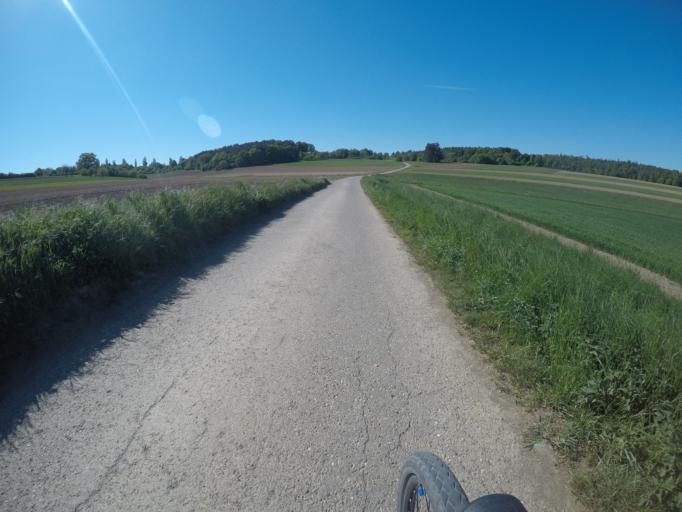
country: DE
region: Baden-Wuerttemberg
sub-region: Karlsruhe Region
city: Heimsheim
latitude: 48.8207
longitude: 8.8536
